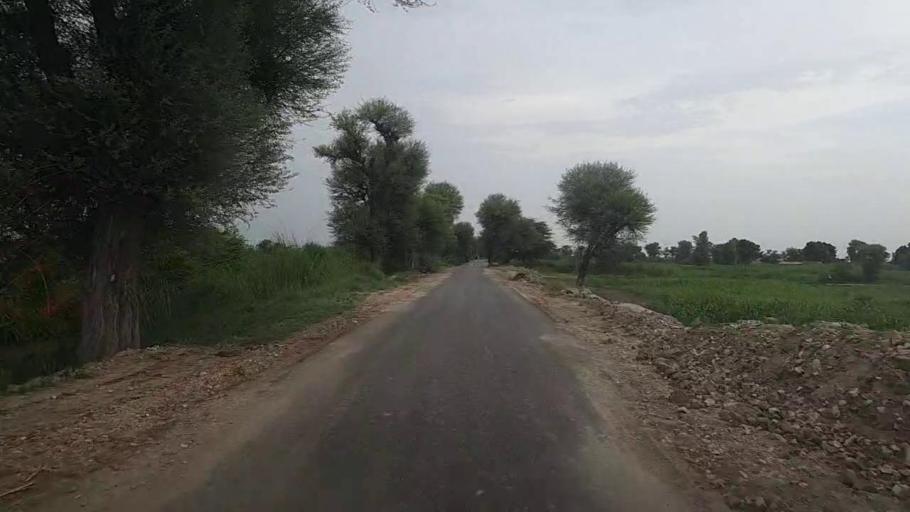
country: PK
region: Sindh
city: Karaundi
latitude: 26.9779
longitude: 68.3583
